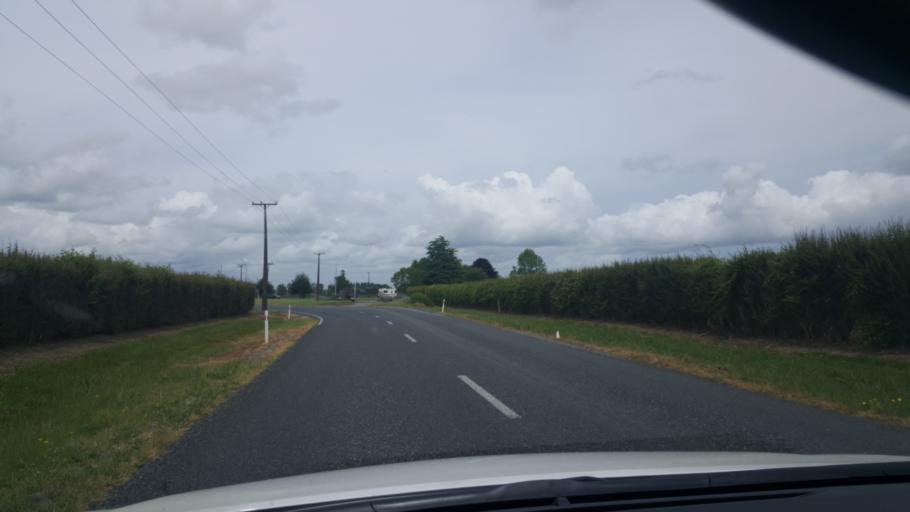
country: NZ
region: Waikato
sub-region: Matamata-Piako District
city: Matamata
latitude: -37.8819
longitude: 175.7312
